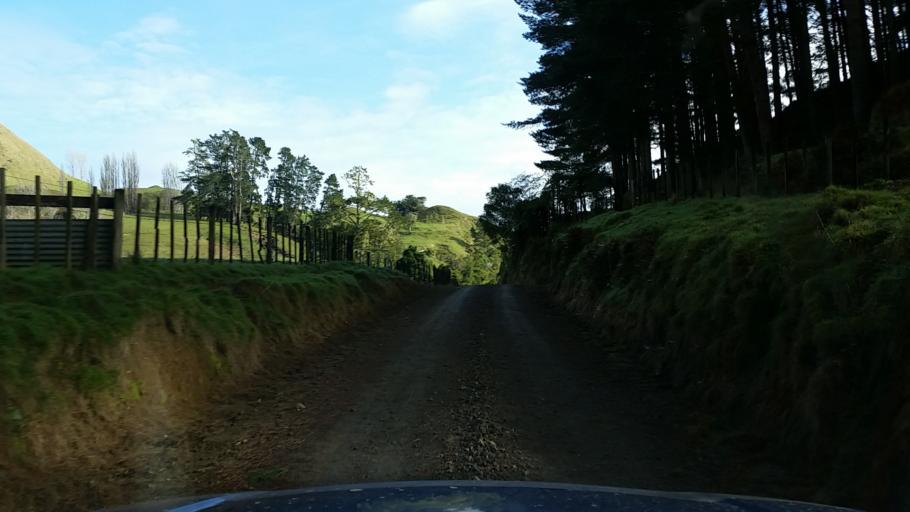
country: NZ
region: Taranaki
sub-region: New Plymouth District
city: Waitara
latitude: -39.1133
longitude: 174.8545
